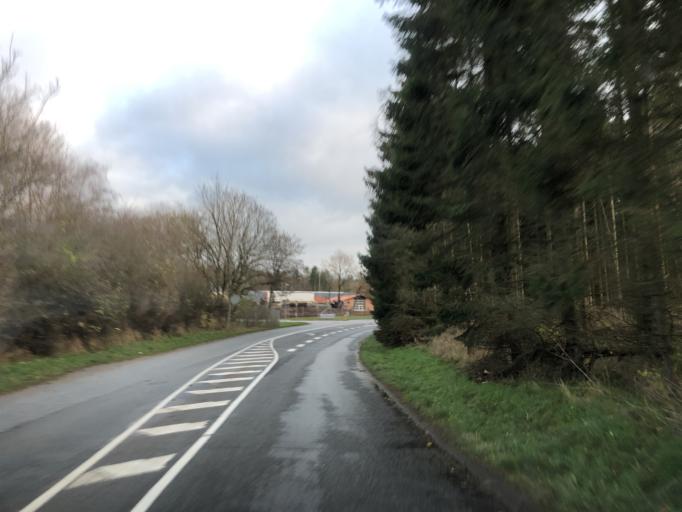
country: DK
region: Central Jutland
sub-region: Viborg Kommune
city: Viborg
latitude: 56.4747
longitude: 9.3562
